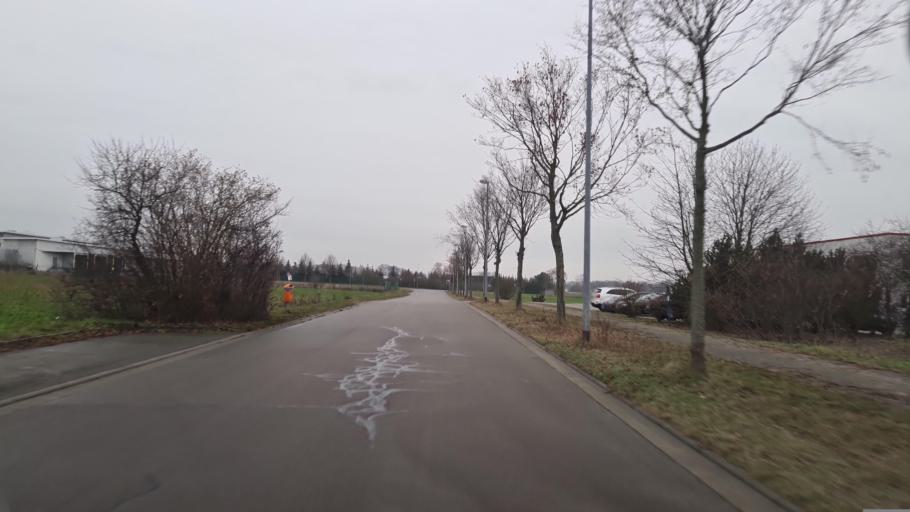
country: DE
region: Brandenburg
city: Werben
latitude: 51.7648
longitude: 14.1585
